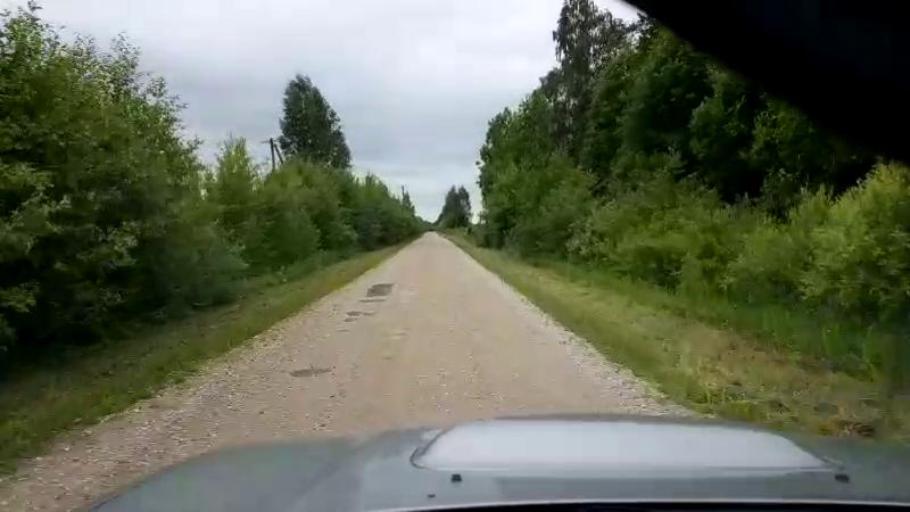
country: EE
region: Paernumaa
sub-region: Halinga vald
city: Parnu-Jaagupi
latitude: 58.5592
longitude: 24.5629
